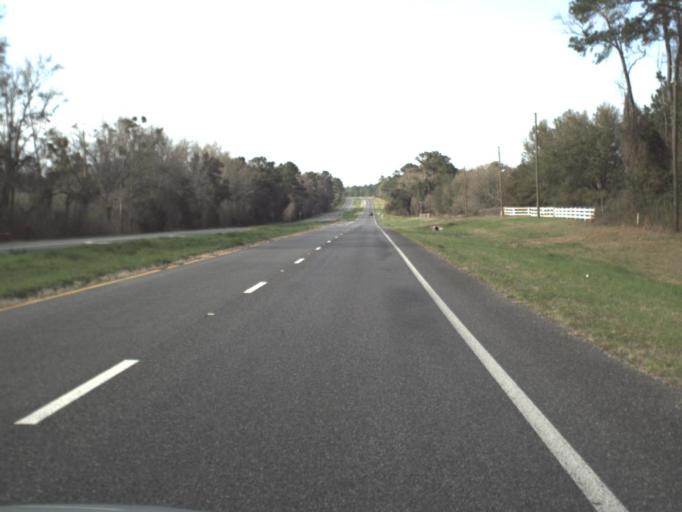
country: US
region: Florida
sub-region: Jefferson County
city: Monticello
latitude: 30.6493
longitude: -83.8758
